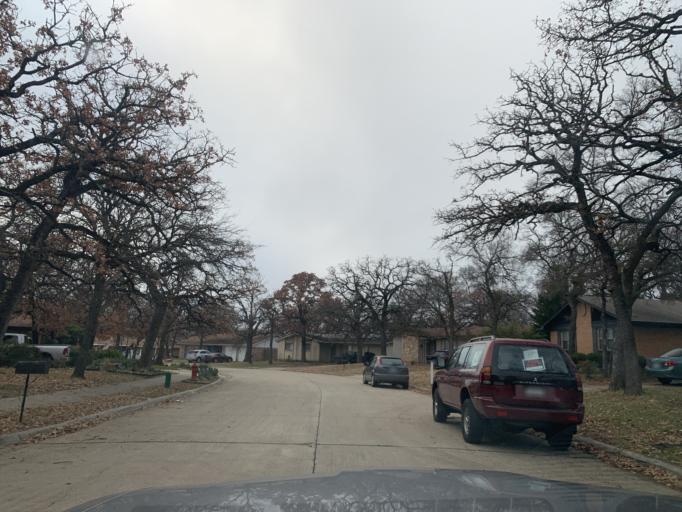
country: US
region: Texas
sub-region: Tarrant County
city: Bedford
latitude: 32.8351
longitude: -97.1563
